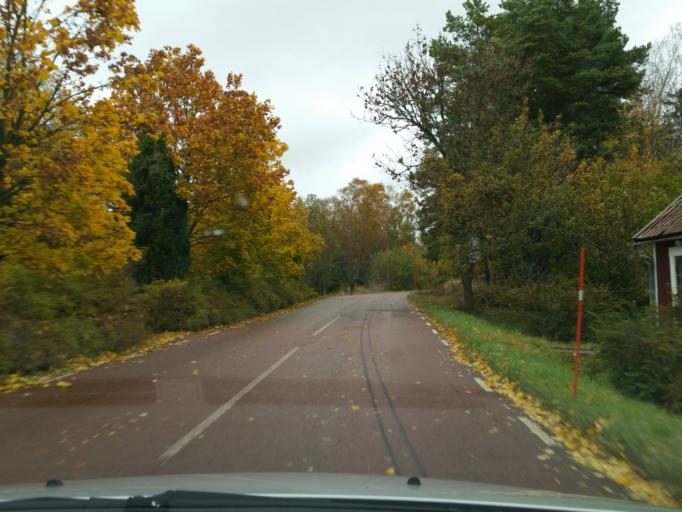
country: AX
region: Alands landsbygd
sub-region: Lumparland
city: Lumparland
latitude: 60.1249
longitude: 20.2399
